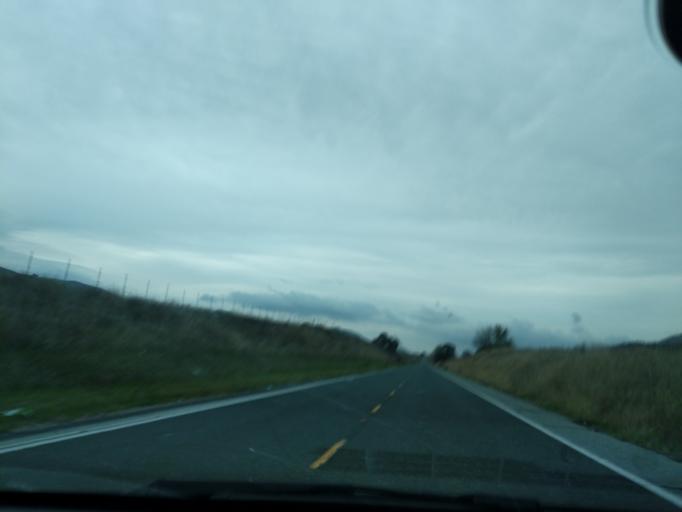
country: US
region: California
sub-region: San Benito County
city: Ridgemark
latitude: 36.6859
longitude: -121.2627
